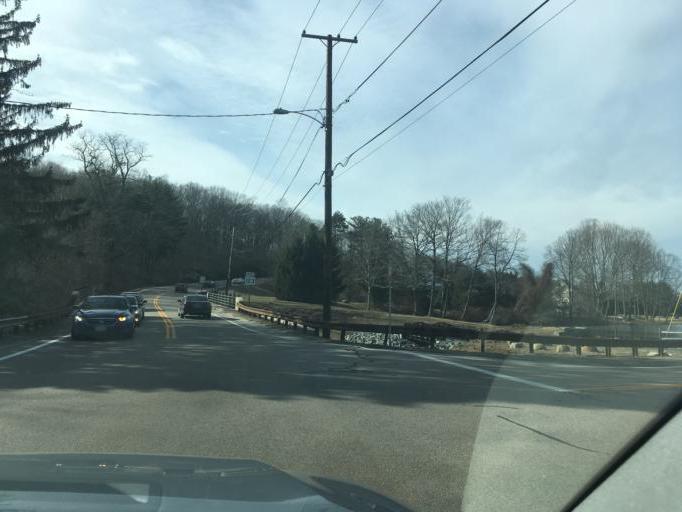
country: US
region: Rhode Island
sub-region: Providence County
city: Valley Falls
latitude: 41.9067
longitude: -71.4314
